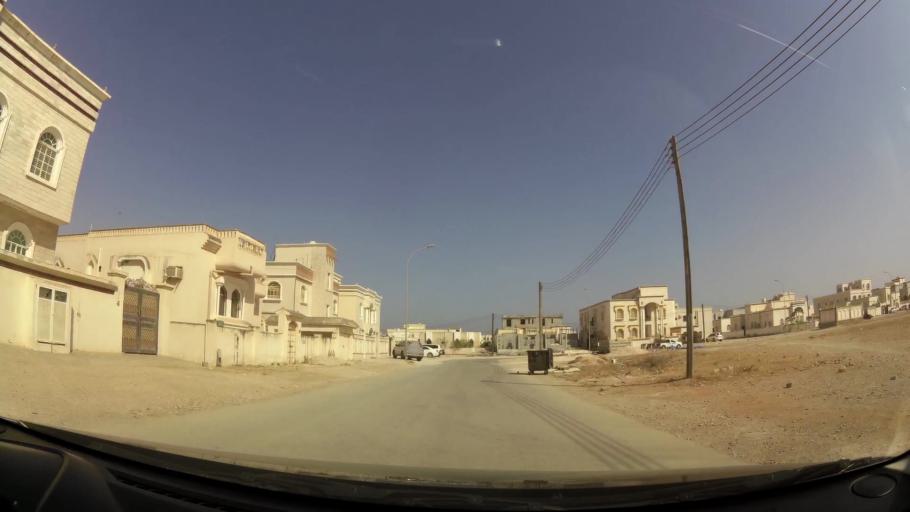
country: OM
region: Zufar
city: Salalah
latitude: 17.0078
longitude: 54.0122
